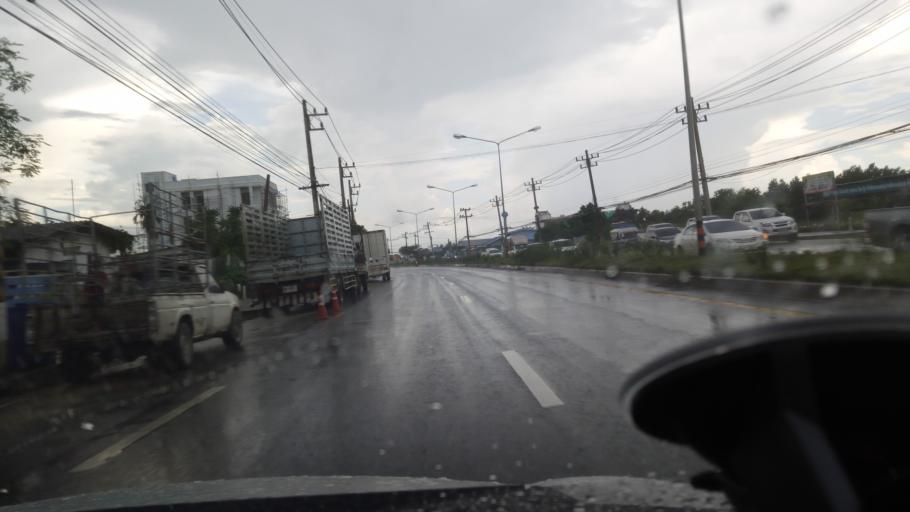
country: TH
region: Chon Buri
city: Phan Thong
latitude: 13.4554
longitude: 101.0964
